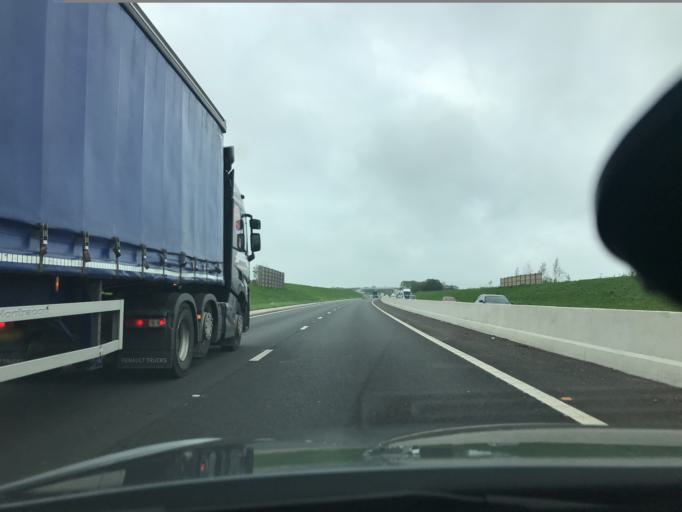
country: GB
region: England
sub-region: Cheshire East
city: Mere
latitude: 53.3516
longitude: -2.4053
